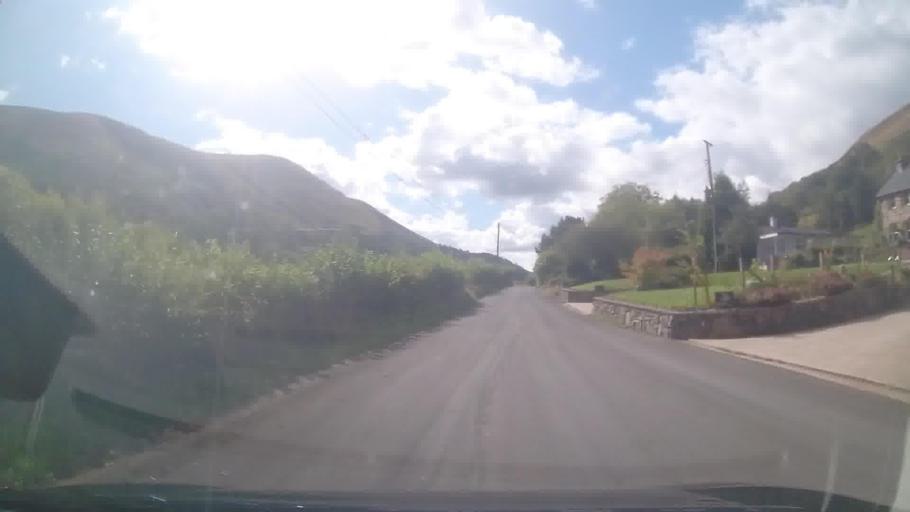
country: GB
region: Wales
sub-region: Gwynedd
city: Bala
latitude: 52.7584
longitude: -3.6246
